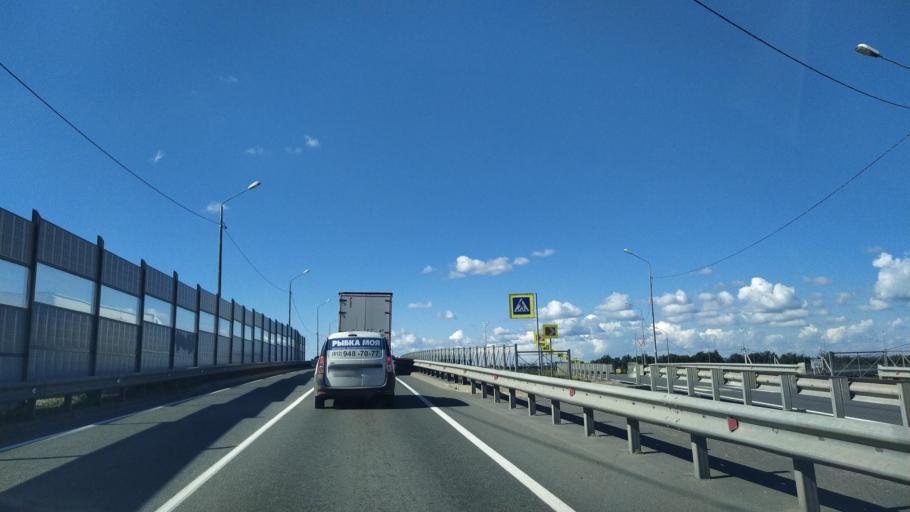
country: RU
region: Leningrad
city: Maloye Verevo
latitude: 59.6126
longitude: 30.1942
